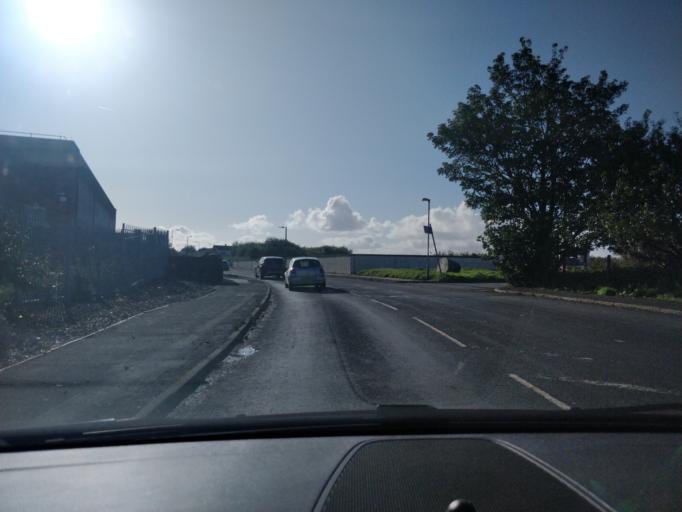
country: GB
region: England
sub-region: Lancashire
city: Banks
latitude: 53.6793
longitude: -2.9436
